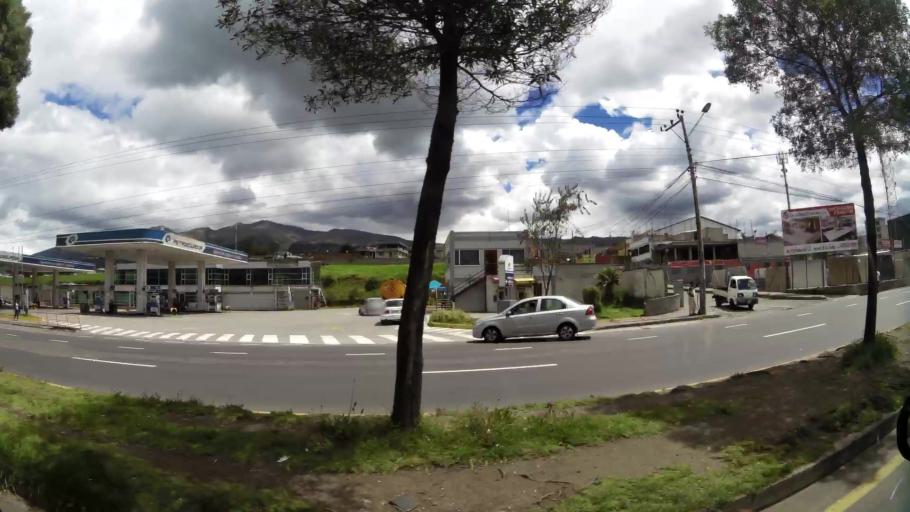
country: EC
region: Pichincha
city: Sangolqui
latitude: -0.3486
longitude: -78.5489
